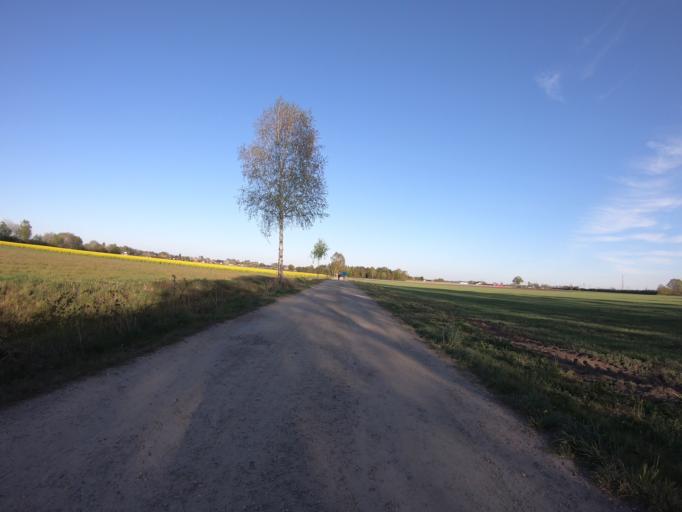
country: DE
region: Lower Saxony
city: Wagenhoff
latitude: 52.5157
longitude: 10.5170
